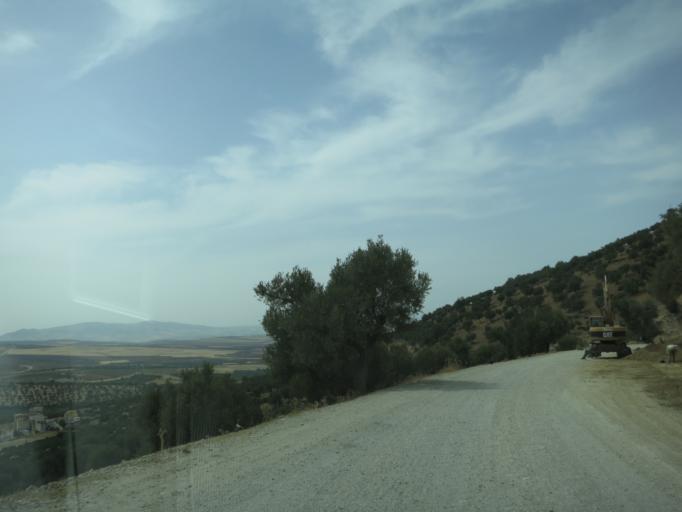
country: MA
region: Meknes-Tafilalet
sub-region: Meknes
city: Meknes
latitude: 34.0597
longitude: -5.5213
